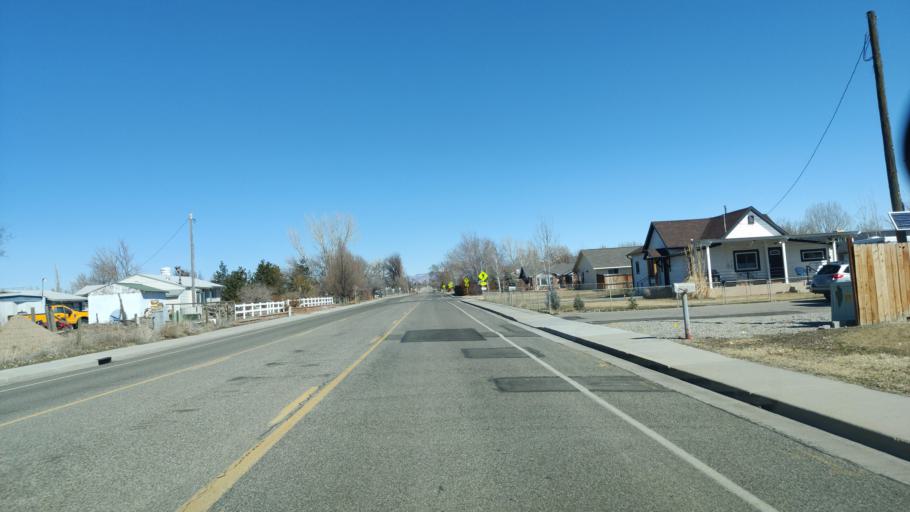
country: US
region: Colorado
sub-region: Mesa County
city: Fruita
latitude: 39.1667
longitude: -108.7197
